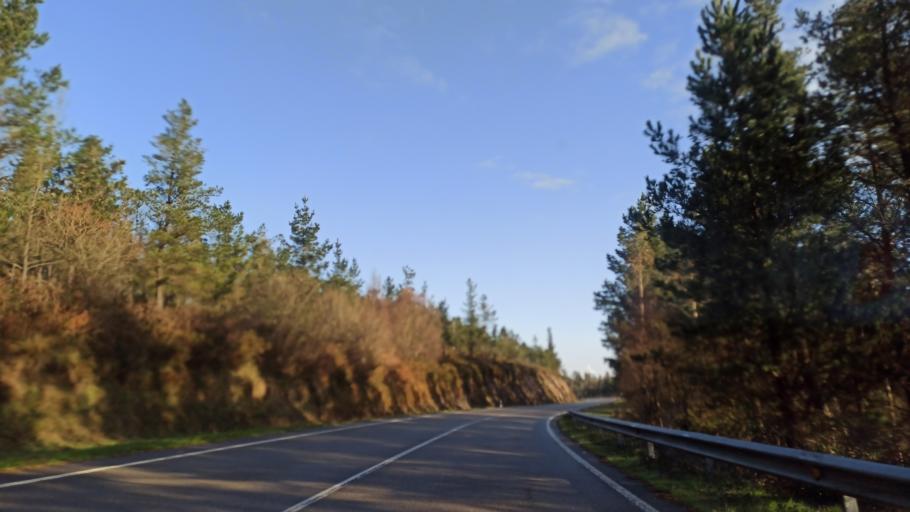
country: ES
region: Galicia
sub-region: Provincia da Coruna
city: As Pontes de Garcia Rodriguez
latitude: 43.4921
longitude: -7.8344
